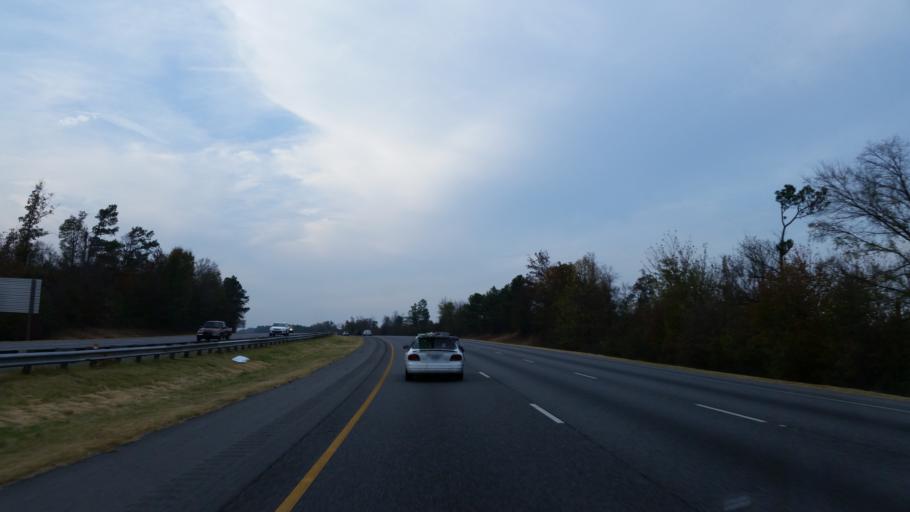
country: US
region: Georgia
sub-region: Bartow County
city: Rydal
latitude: 34.2943
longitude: -84.8227
